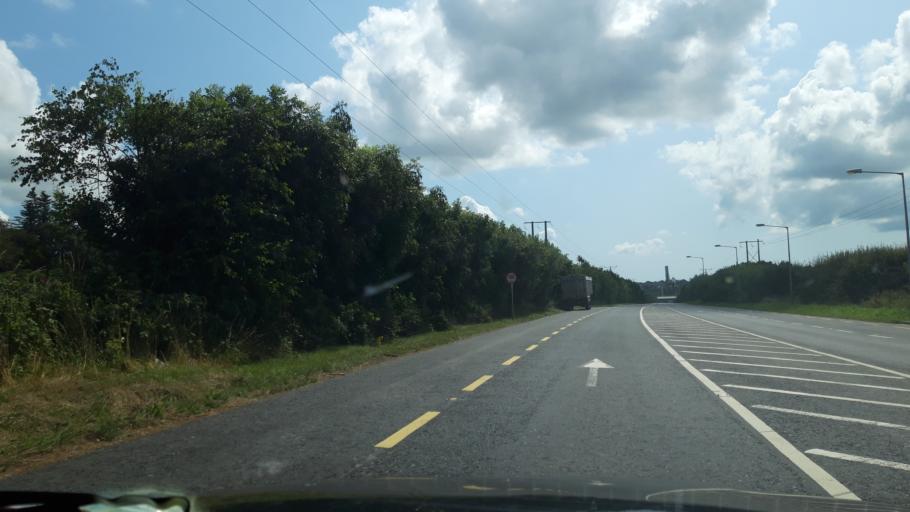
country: IE
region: Munster
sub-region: Waterford
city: Waterford
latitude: 52.2710
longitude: -7.0449
